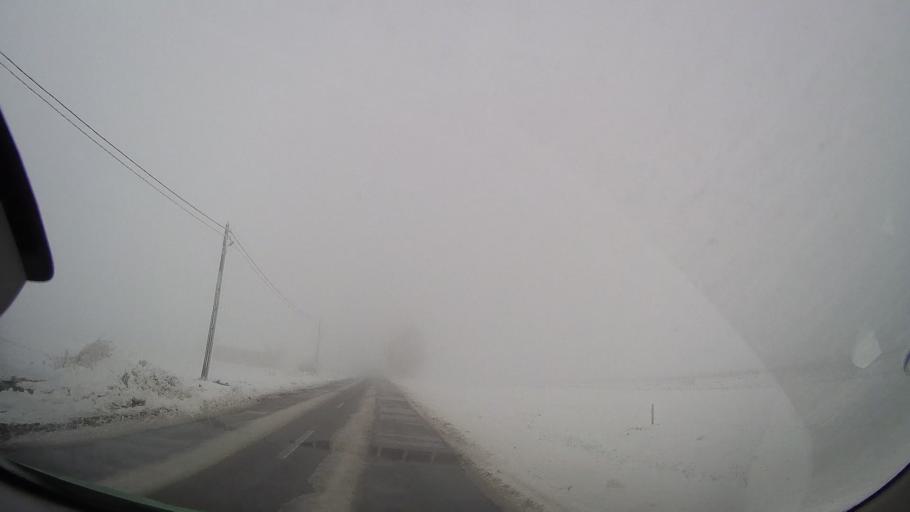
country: RO
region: Neamt
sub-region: Comuna Sabaoani
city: Sabaoani
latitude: 47.0293
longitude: 26.8589
